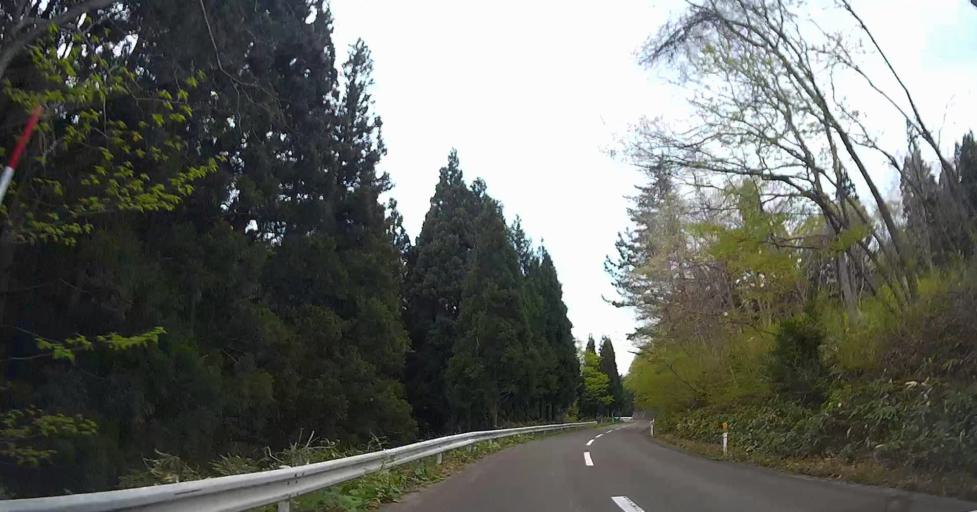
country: JP
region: Aomori
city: Goshogawara
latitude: 40.9028
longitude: 140.5004
